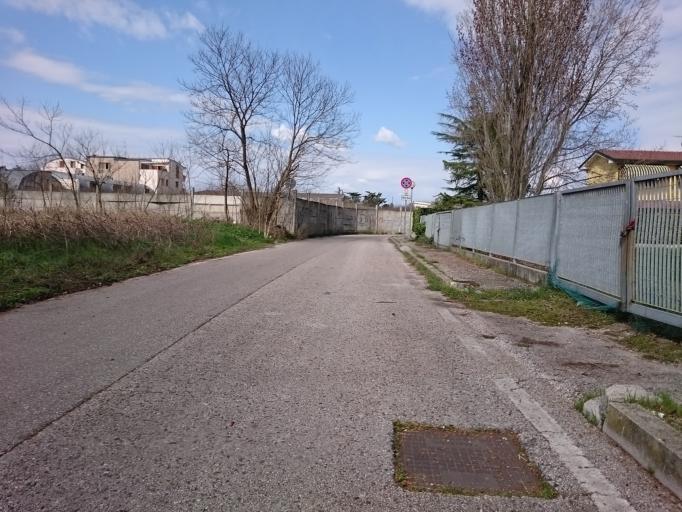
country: IT
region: Veneto
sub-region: Provincia di Padova
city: Mandriola-Sant'Agostino
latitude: 45.3816
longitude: 11.8617
